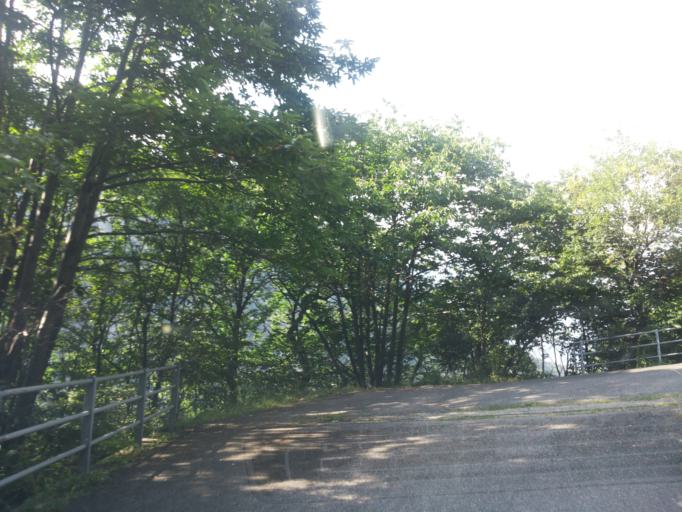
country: IT
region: Aosta Valley
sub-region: Valle d'Aosta
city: Fontainemore
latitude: 45.6408
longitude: 7.8576
